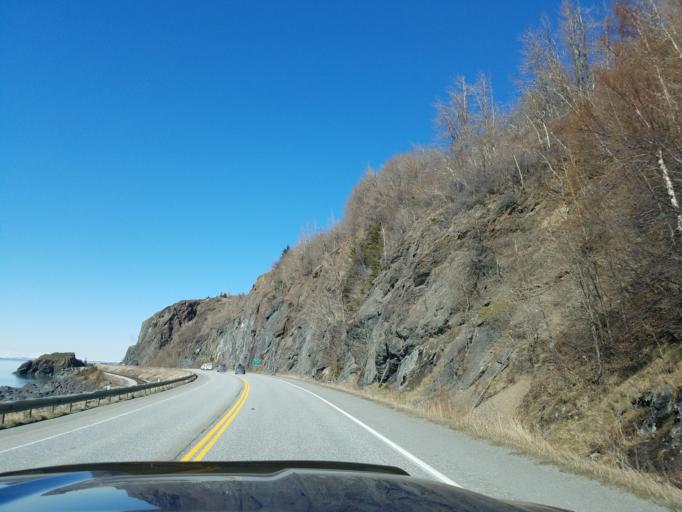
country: US
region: Alaska
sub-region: Anchorage Municipality
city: Anchorage
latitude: 61.0333
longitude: -149.7689
